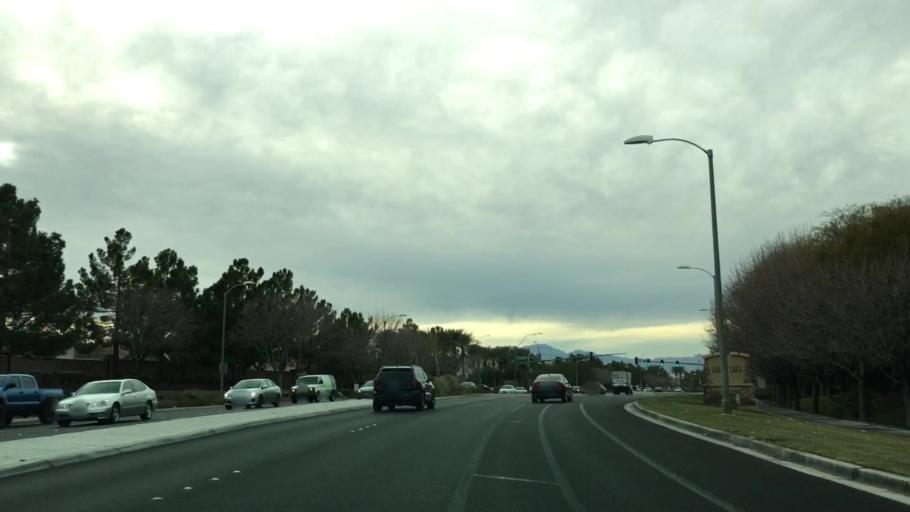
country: US
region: Nevada
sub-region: Clark County
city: Whitney
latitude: 36.0182
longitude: -115.0892
